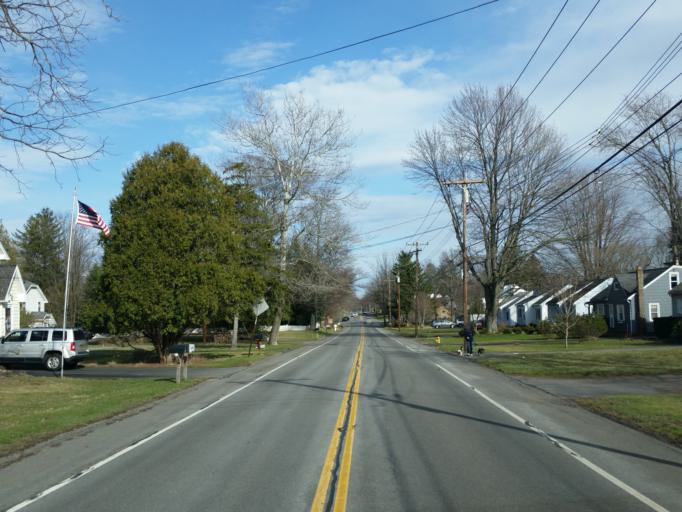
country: US
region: New York
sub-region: Monroe County
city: North Gates
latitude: 43.1162
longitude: -77.7486
